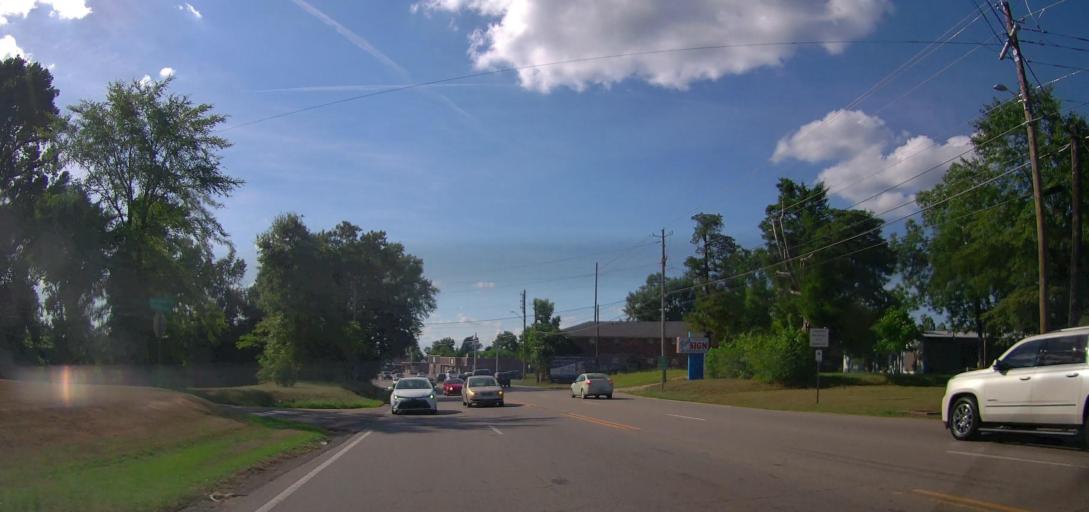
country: US
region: Alabama
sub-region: Tuscaloosa County
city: Holt
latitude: 33.2042
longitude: -87.4889
